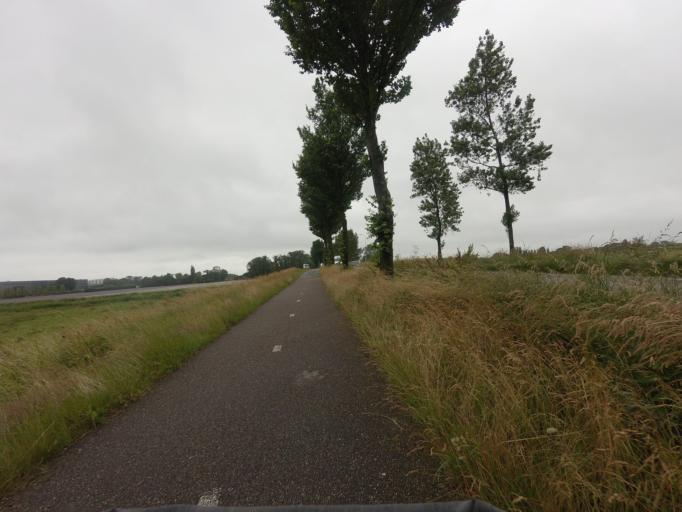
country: NL
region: North Holland
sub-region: Gemeente Opmeer
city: Opmeer
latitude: 52.7636
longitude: 4.8908
